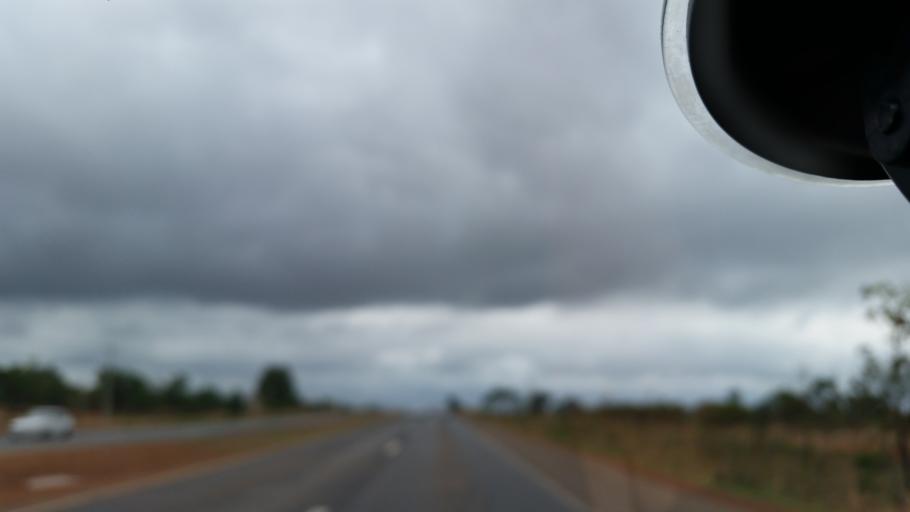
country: BR
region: Goias
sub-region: Luziania
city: Luziania
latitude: -16.3180
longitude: -47.8410
